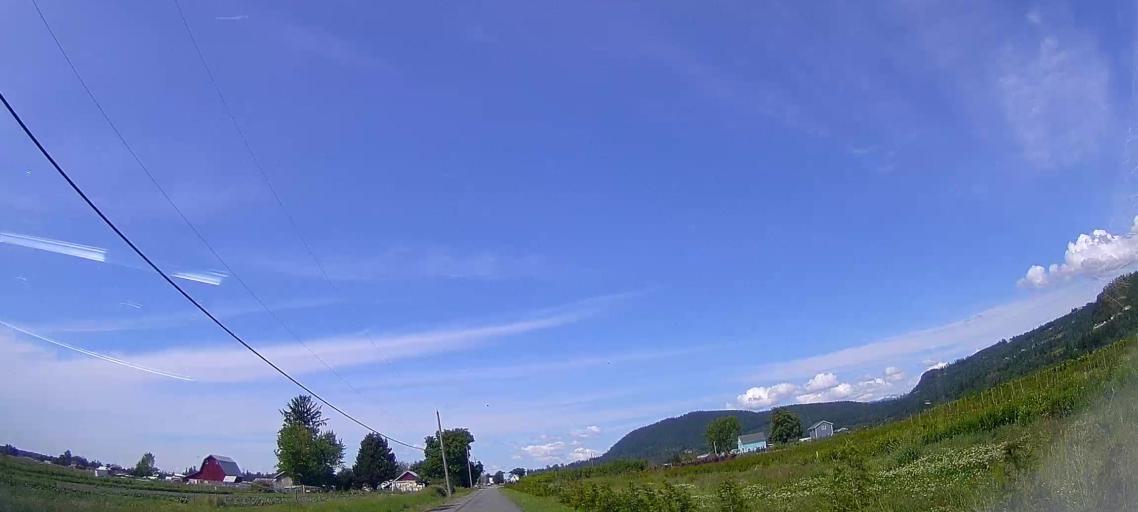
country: US
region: Washington
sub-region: Skagit County
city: Mount Vernon
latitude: 48.3605
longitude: -122.3235
